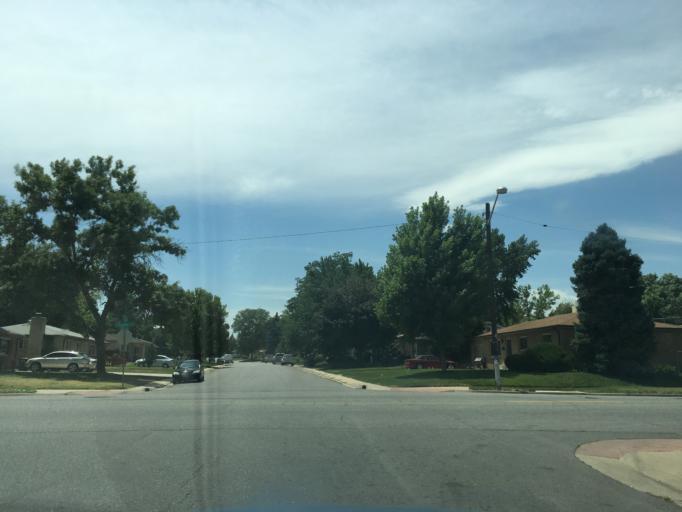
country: US
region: Colorado
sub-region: Arapahoe County
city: Sheridan
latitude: 39.6789
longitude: -105.0365
